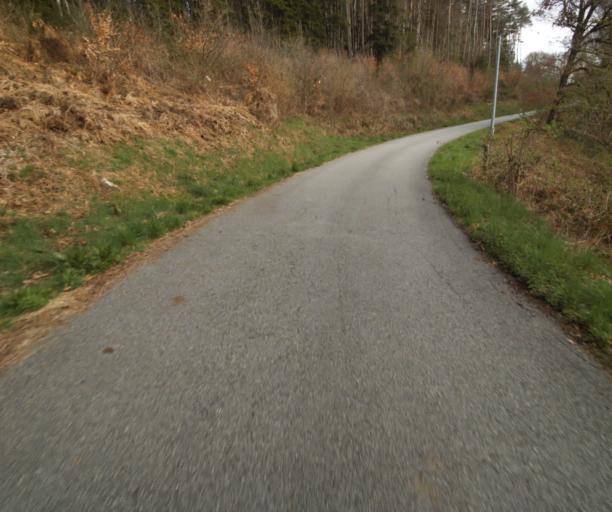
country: FR
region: Limousin
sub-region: Departement de la Correze
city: Correze
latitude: 45.3836
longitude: 1.8766
